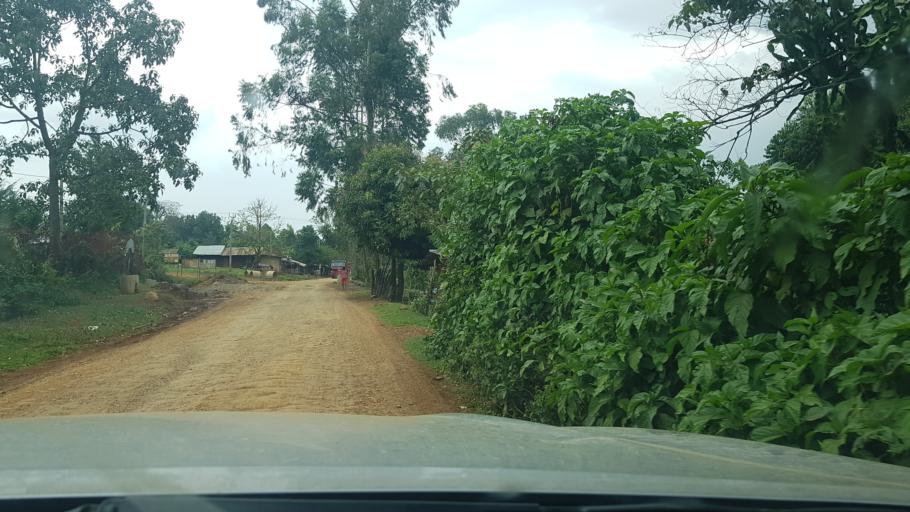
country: ET
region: Oromiya
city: Gore
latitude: 7.8337
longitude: 35.4685
